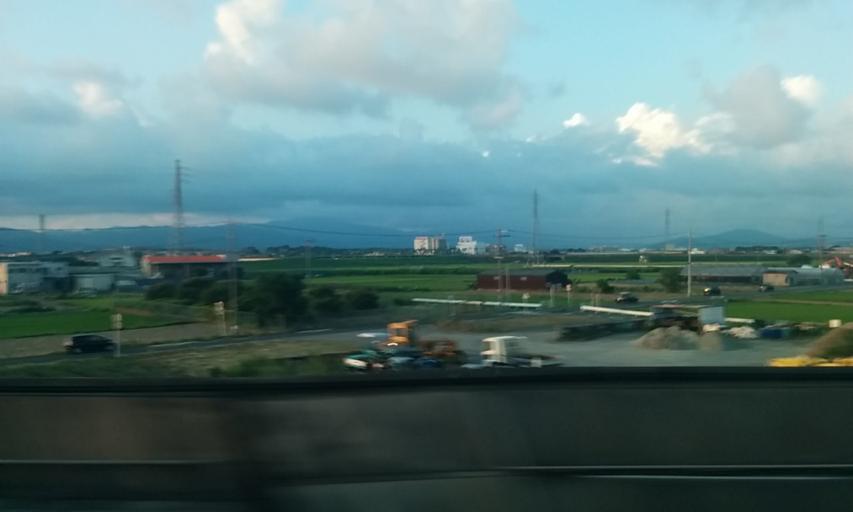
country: JP
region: Aichi
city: Kozakai-cho
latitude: 34.7850
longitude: 137.3601
